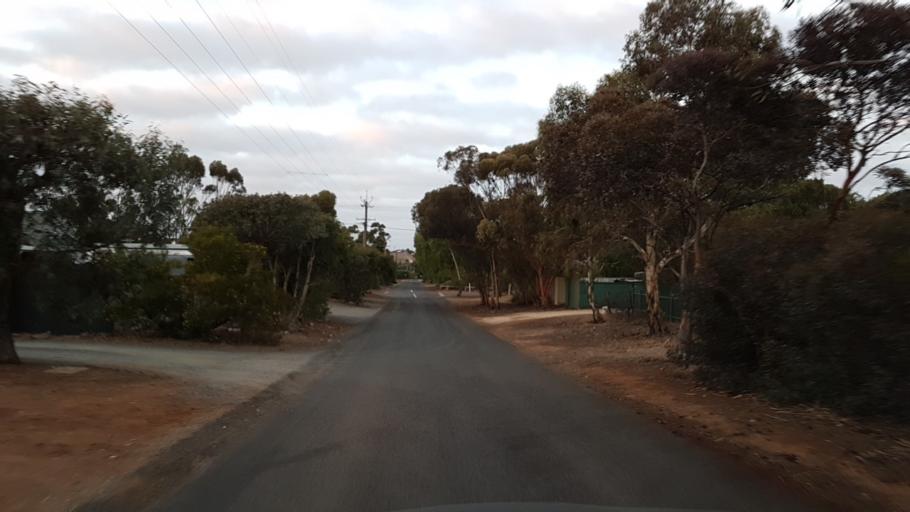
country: AU
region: South Australia
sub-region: Mount Barker
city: Callington
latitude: -35.0700
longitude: 139.0116
